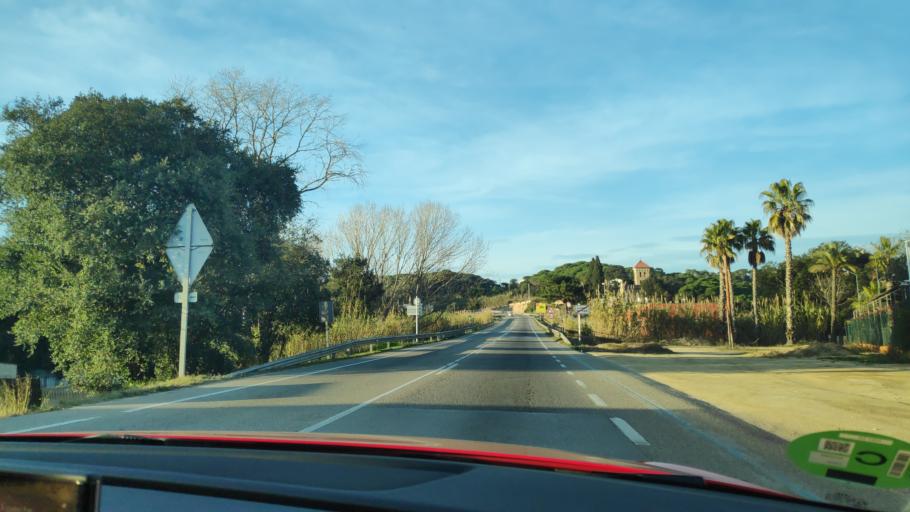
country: ES
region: Catalonia
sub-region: Provincia de Girona
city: Lloret de Mar
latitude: 41.7153
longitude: 2.8303
